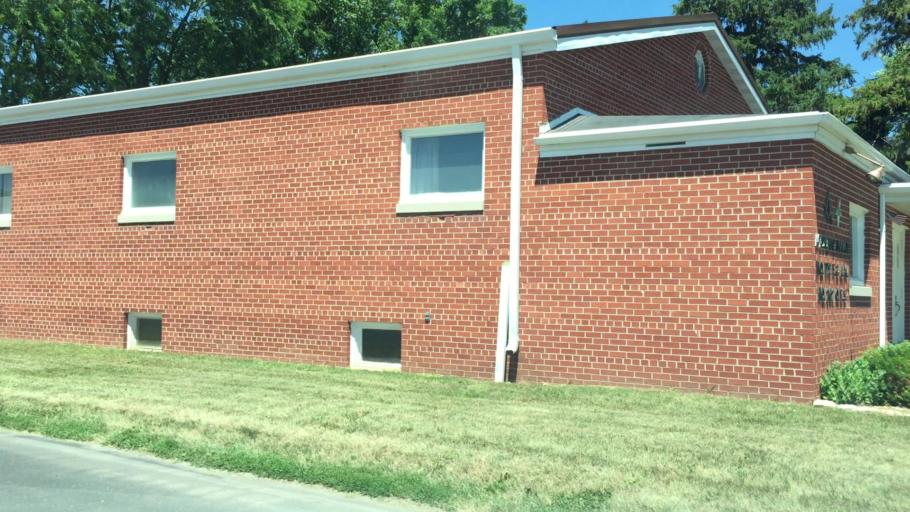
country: US
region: Wisconsin
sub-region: Calumet County
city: New Holstein
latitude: 43.9503
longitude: -88.0960
